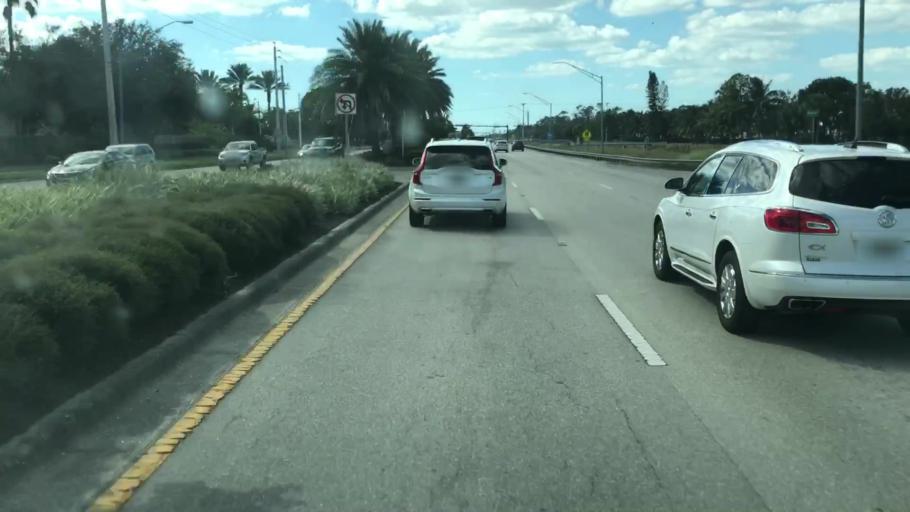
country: US
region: Florida
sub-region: Collier County
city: Vineyards
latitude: 26.2730
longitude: -81.7020
